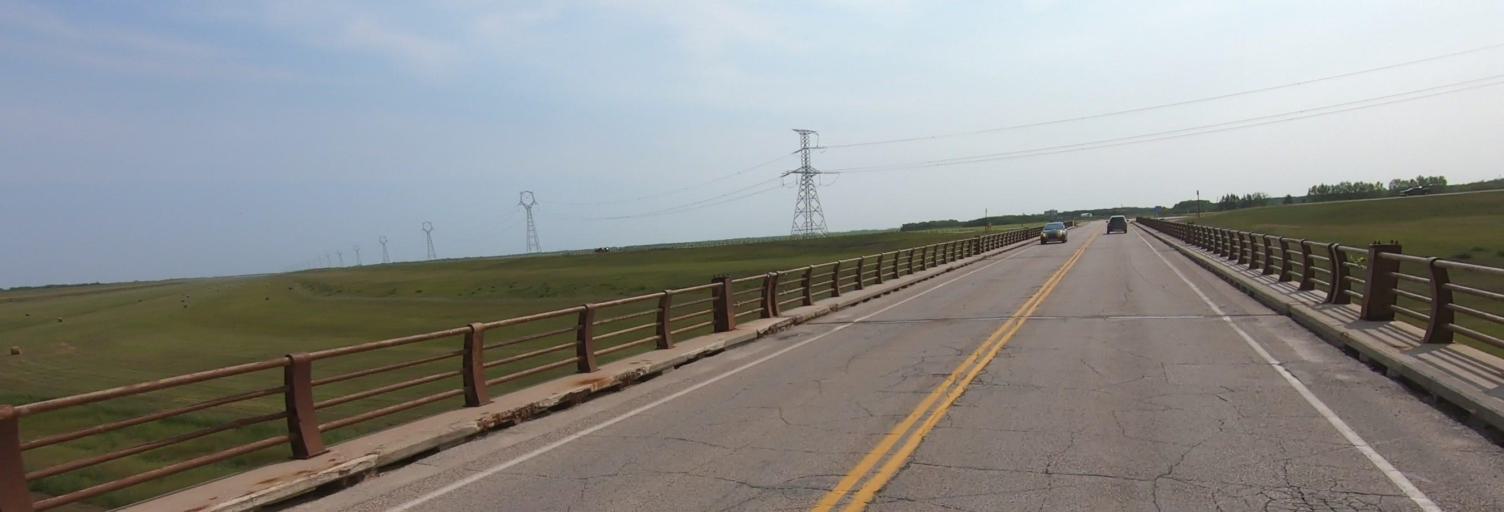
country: CA
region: Manitoba
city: Winnipeg
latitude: 49.7568
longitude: -97.1216
